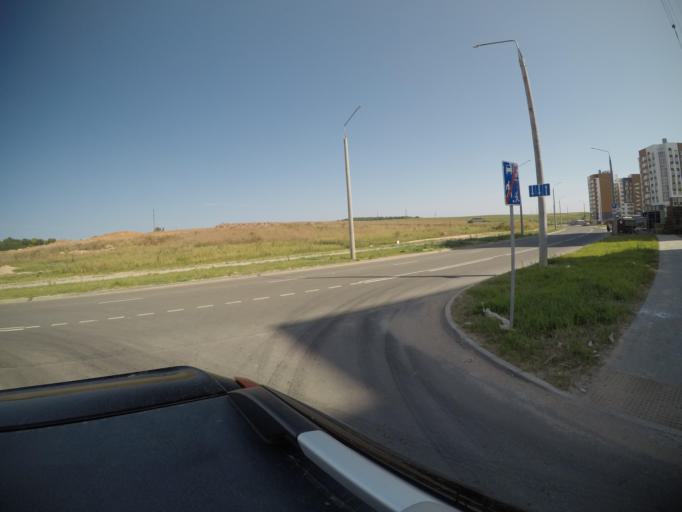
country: BY
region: Grodnenskaya
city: Hrodna
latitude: 53.7226
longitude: 23.8816
